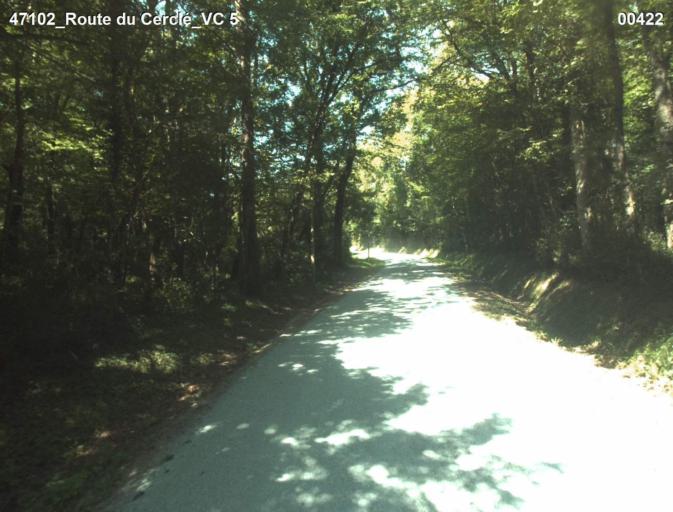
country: FR
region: Aquitaine
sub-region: Departement du Lot-et-Garonne
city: Laplume
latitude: 44.0727
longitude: 0.4568
